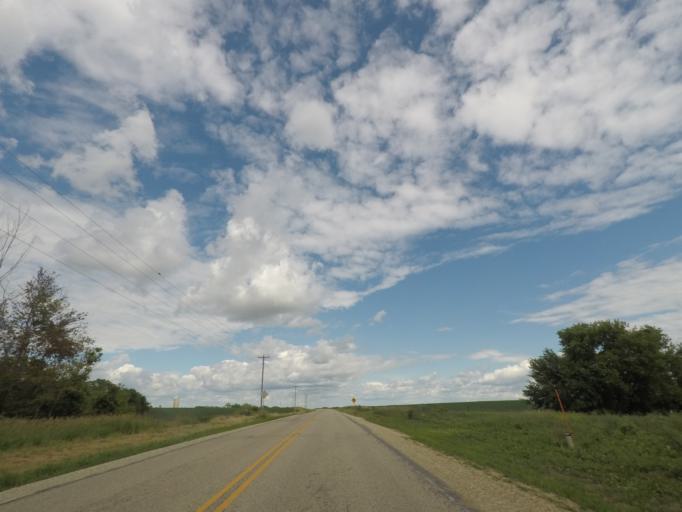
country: US
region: Wisconsin
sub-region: Rock County
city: Orfordville
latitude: 42.7154
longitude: -89.2380
